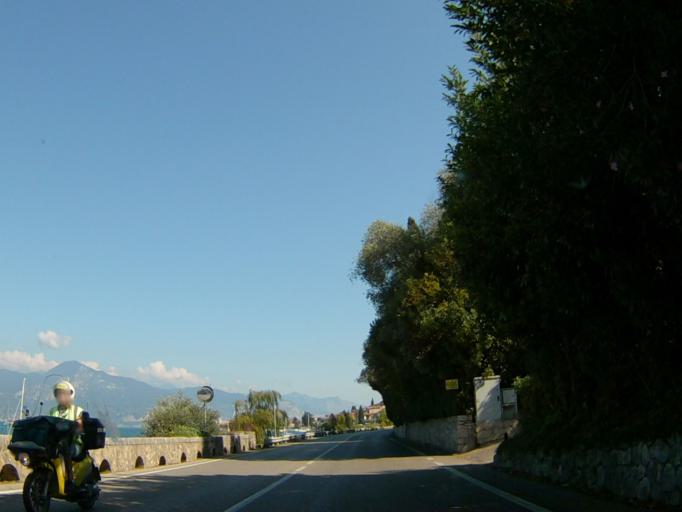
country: IT
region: Veneto
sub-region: Provincia di Verona
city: Torri del Benaco
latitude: 45.5958
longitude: 10.6826
